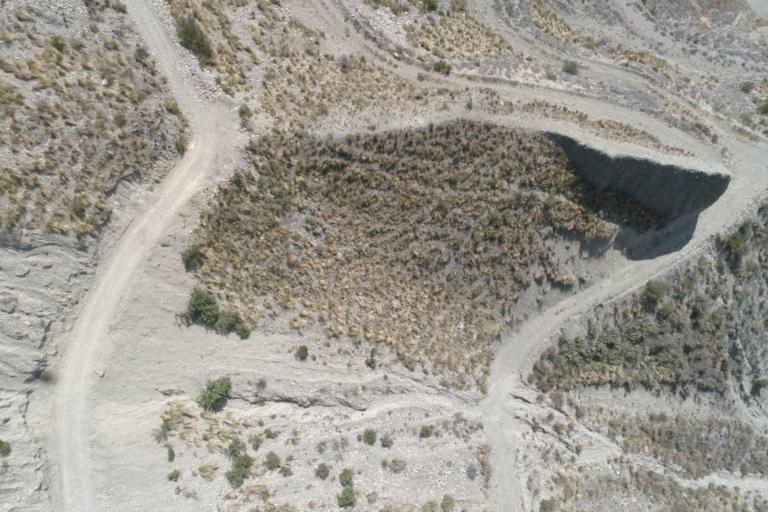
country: BO
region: La Paz
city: La Paz
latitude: -16.4735
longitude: -68.0992
